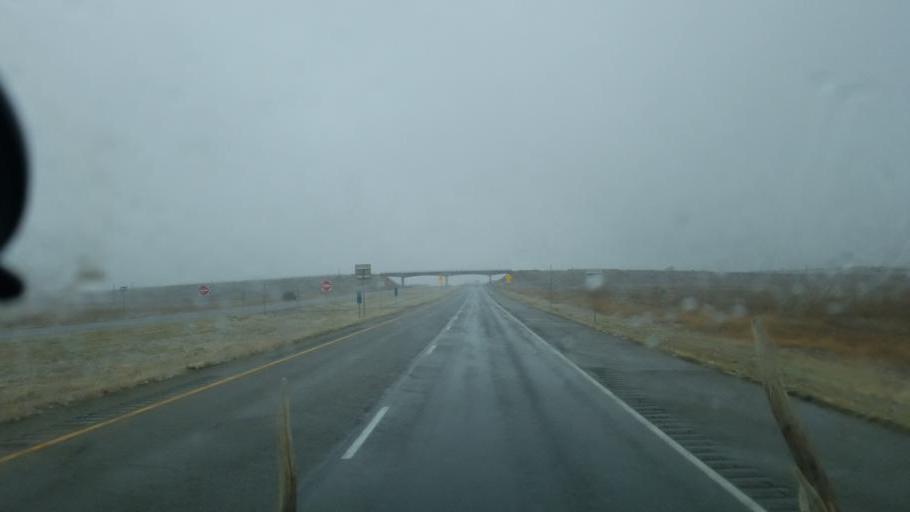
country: US
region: Colorado
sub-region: Pueblo County
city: Colorado City
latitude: 37.8912
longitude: -104.8287
